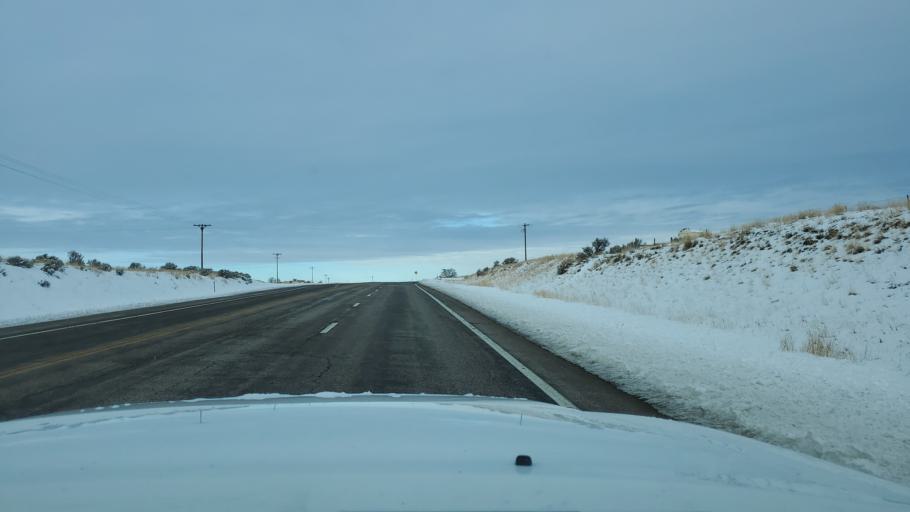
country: US
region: Colorado
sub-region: Moffat County
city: Craig
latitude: 40.5091
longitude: -107.6851
